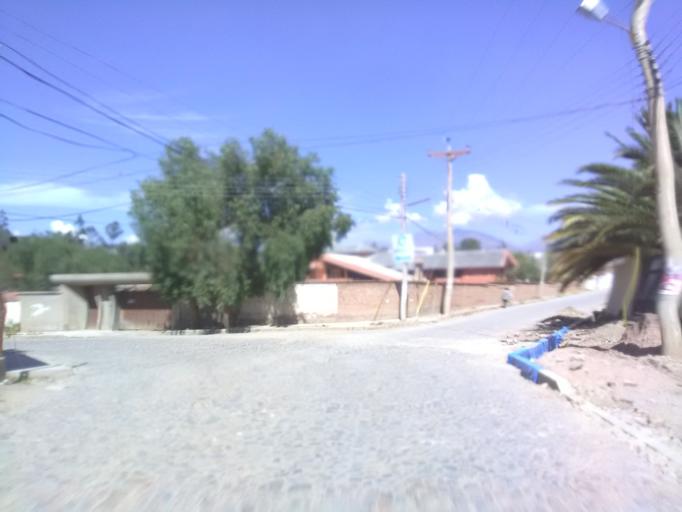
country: BO
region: Cochabamba
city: Cochabamba
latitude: -17.3527
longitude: -66.2005
